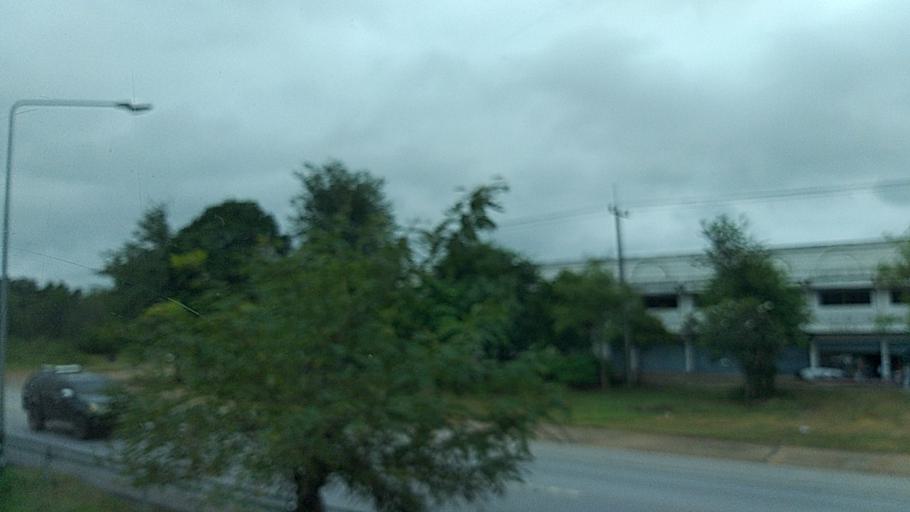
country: TH
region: Nakhon Ratchasima
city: Sida
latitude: 15.5340
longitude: 102.5448
